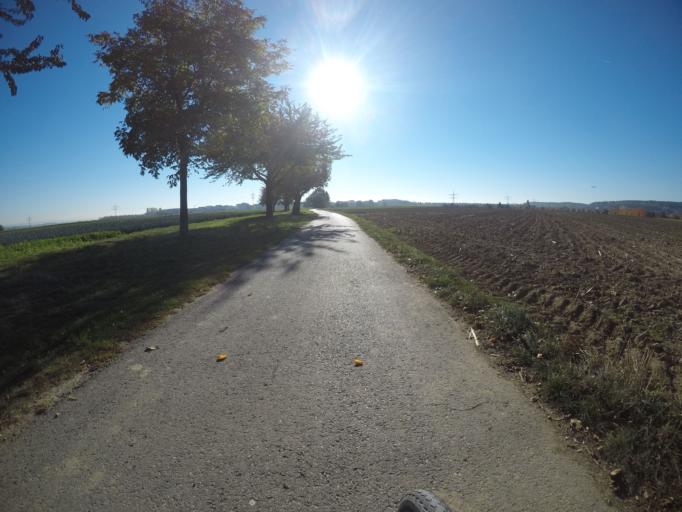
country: DE
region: Baden-Wuerttemberg
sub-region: Regierungsbezirk Stuttgart
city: Leinfelden-Echterdingen
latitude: 48.6995
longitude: 9.1510
